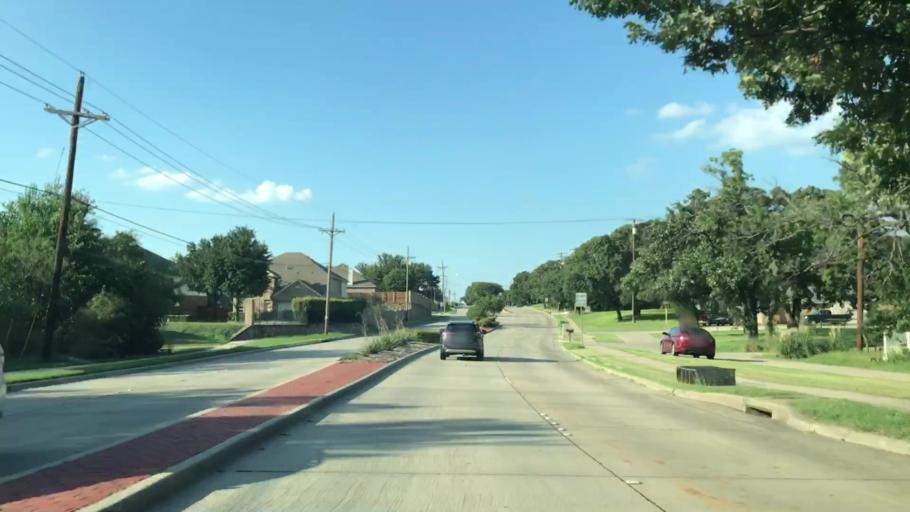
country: US
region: Texas
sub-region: Denton County
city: Lewisville
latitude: 33.0228
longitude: -97.0193
